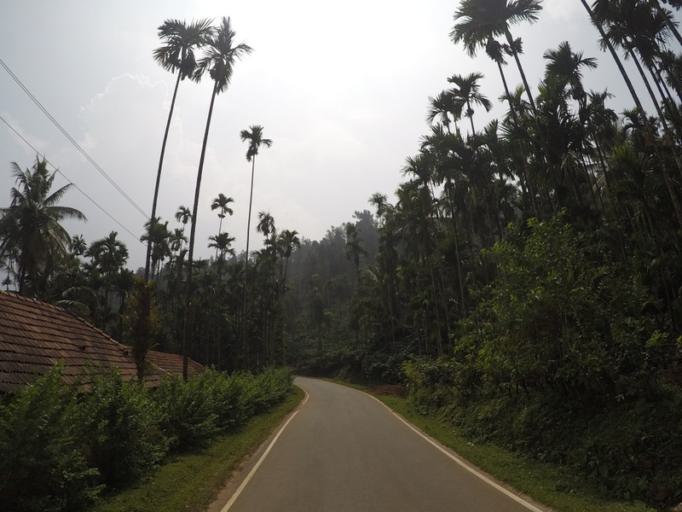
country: IN
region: Karnataka
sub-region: Chikmagalur
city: Mudigere
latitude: 13.1973
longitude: 75.3912
